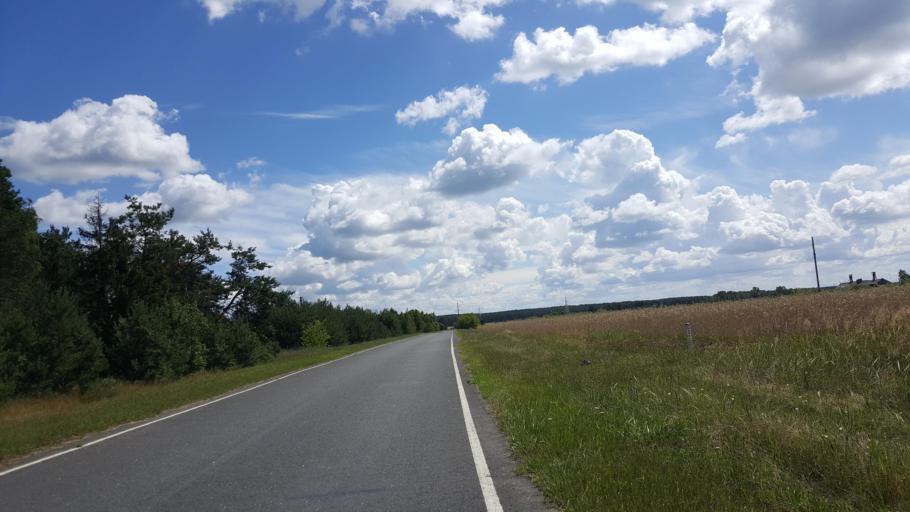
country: BY
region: Brest
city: Kamyanyets
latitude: 52.3403
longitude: 23.8996
